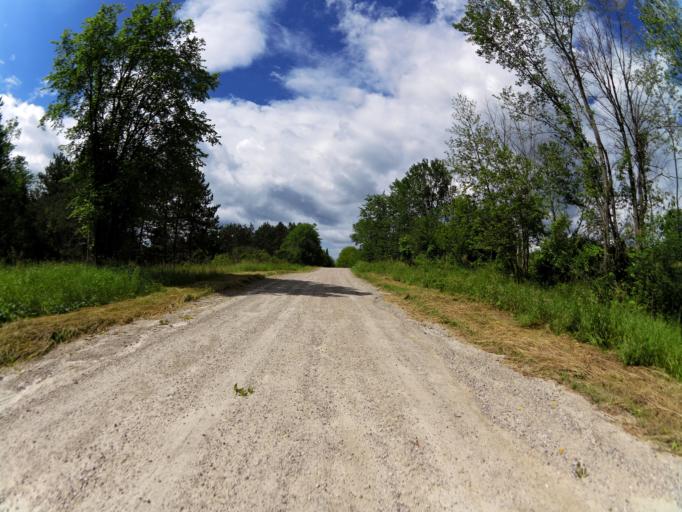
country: CA
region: Ontario
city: Perth
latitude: 45.0278
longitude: -76.5101
